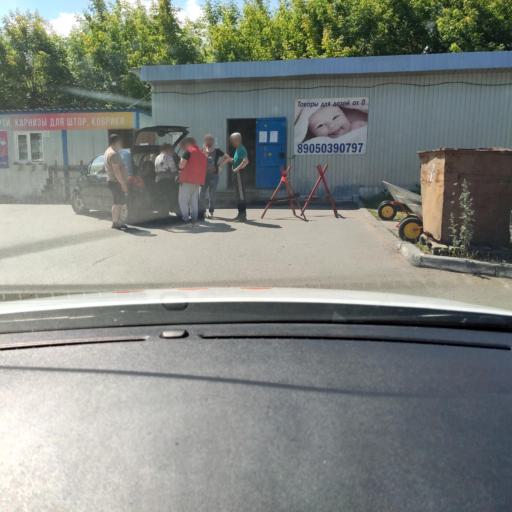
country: RU
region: Tatarstan
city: Staroye Arakchino
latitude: 55.8528
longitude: 49.0263
